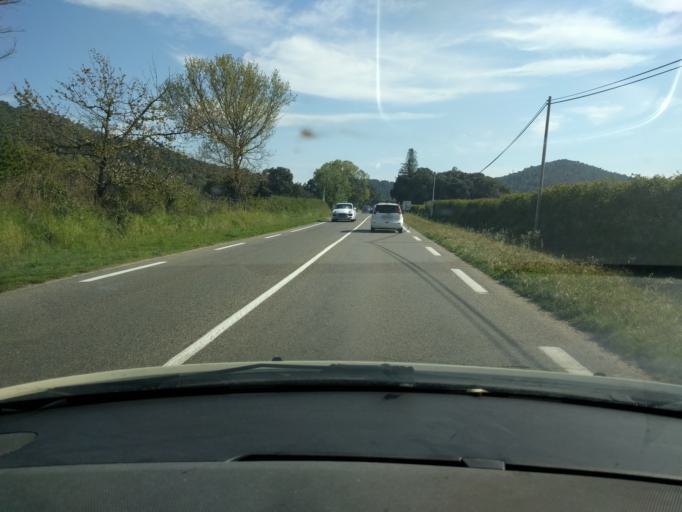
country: FR
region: Provence-Alpes-Cote d'Azur
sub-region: Departement du Var
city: La Crau
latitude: 43.1750
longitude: 6.1179
